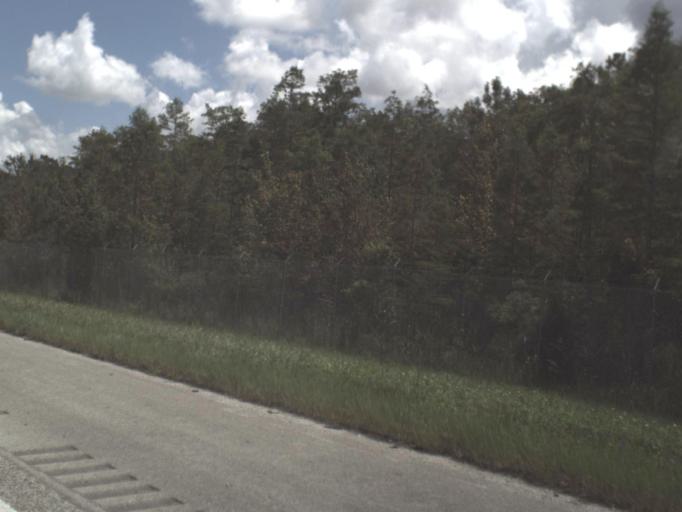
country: US
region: Florida
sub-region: Collier County
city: Immokalee
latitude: 26.1566
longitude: -81.2558
